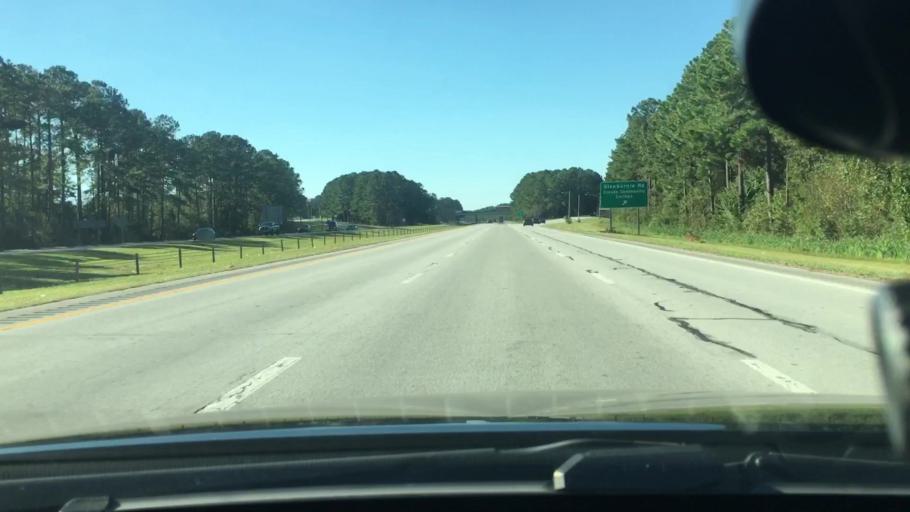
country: US
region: North Carolina
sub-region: Craven County
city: Trent Woods
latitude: 35.1094
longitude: -77.0923
